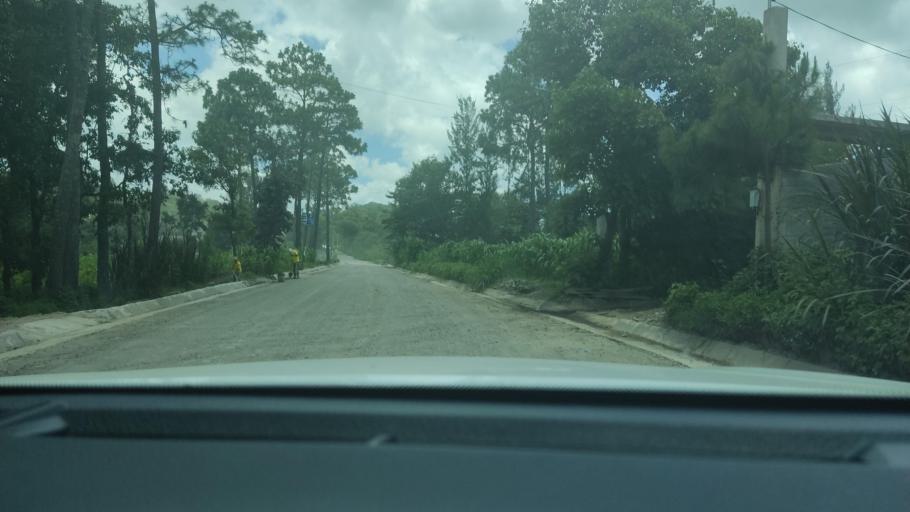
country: GT
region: Chimaltenango
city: San Martin Jilotepeque
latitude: 14.7979
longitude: -90.8147
